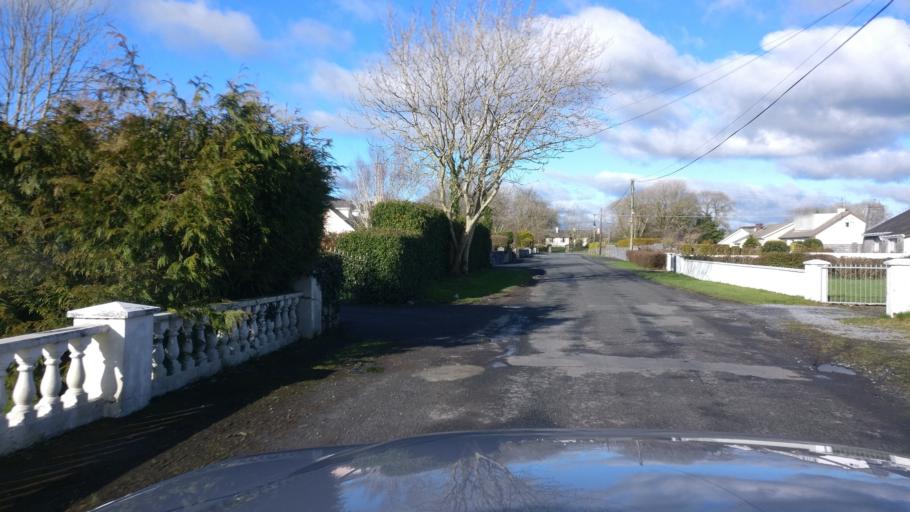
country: IE
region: Connaught
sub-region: County Galway
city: Oranmore
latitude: 53.2774
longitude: -8.9063
